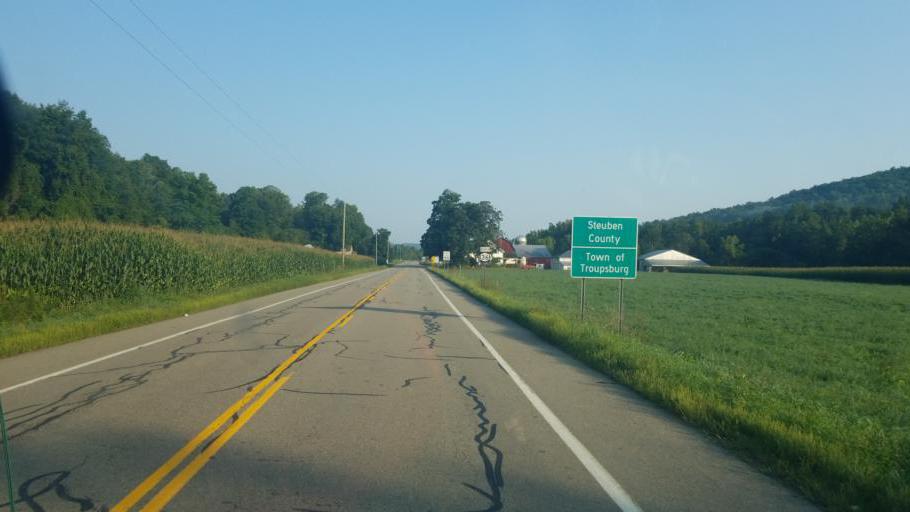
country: US
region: Pennsylvania
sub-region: Tioga County
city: Westfield
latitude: 42.0001
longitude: -77.5040
